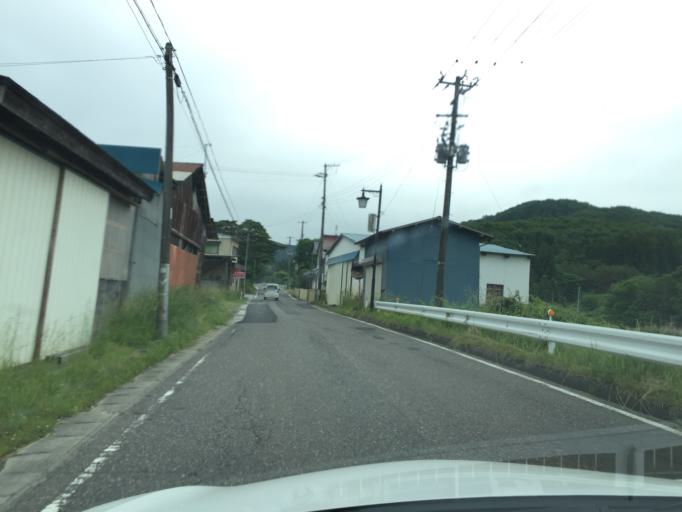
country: JP
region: Fukushima
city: Funehikimachi-funehiki
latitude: 37.3702
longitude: 140.6386
